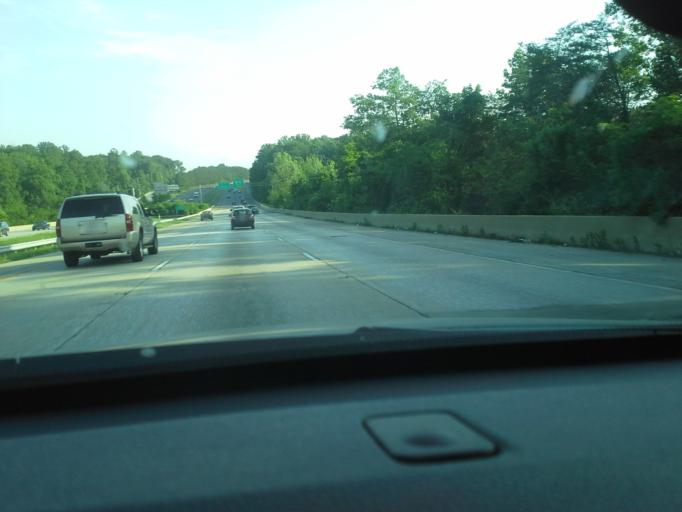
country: US
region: Maryland
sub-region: Anne Arundel County
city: Gambrills
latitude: 39.0830
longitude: -76.6260
